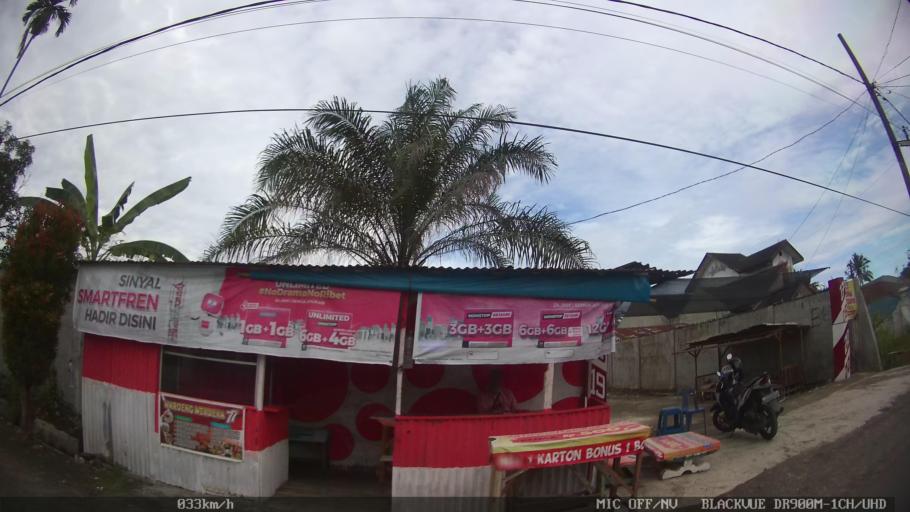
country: ID
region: North Sumatra
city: Sunggal
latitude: 3.5974
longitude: 98.5660
